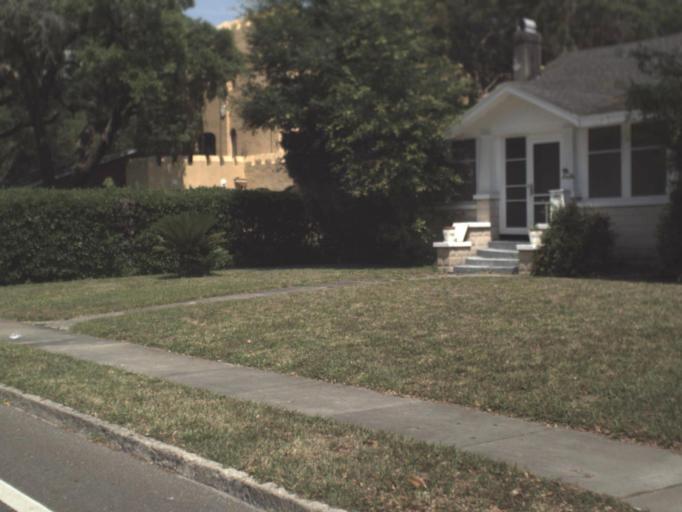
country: US
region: Florida
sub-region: Saint Johns County
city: Saint Augustine
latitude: 29.9099
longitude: -81.3176
